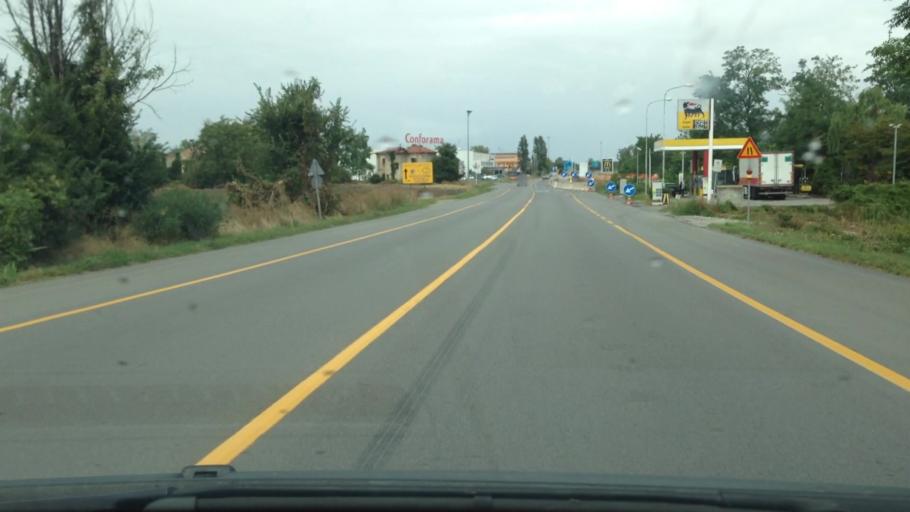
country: IT
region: Piedmont
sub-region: Provincia di Alessandria
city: Tortona
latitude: 44.9000
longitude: 8.8393
